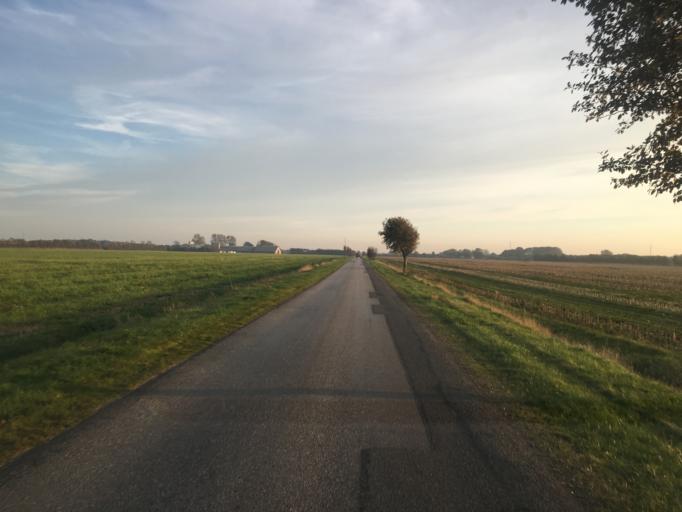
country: DK
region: South Denmark
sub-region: Tonder Kommune
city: Logumkloster
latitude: 55.0479
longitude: 9.0248
